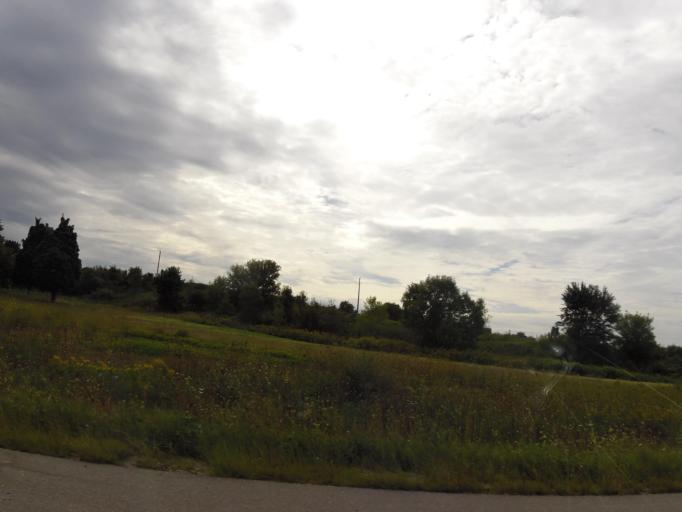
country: US
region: Wisconsin
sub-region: La Crosse County
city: West Salem
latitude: 43.8855
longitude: -91.1093
